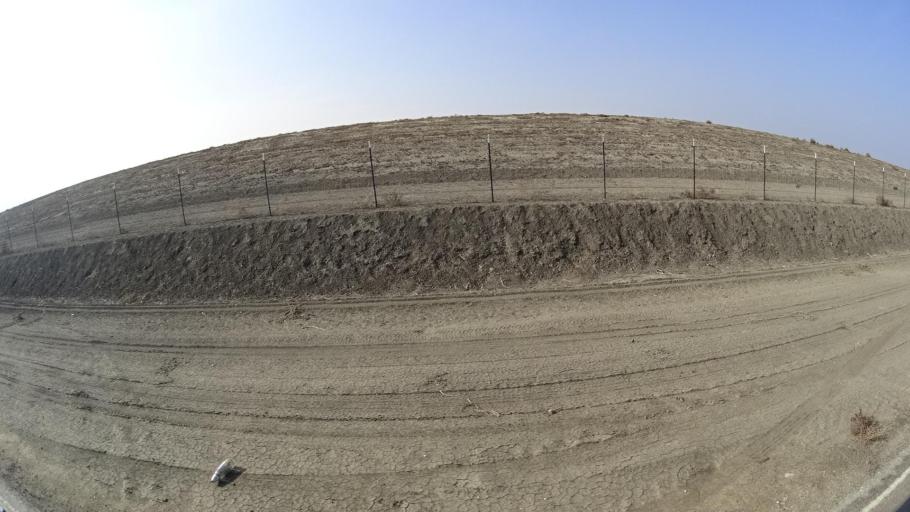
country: US
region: California
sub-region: Kern County
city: Buttonwillow
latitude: 35.3168
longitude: -119.3768
